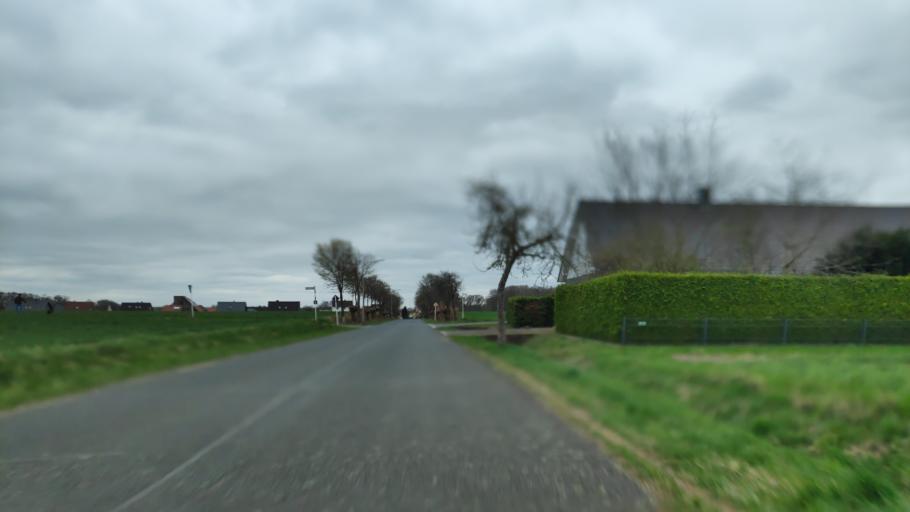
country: DE
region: North Rhine-Westphalia
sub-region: Regierungsbezirk Detmold
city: Petershagen
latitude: 52.3502
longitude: 8.9307
